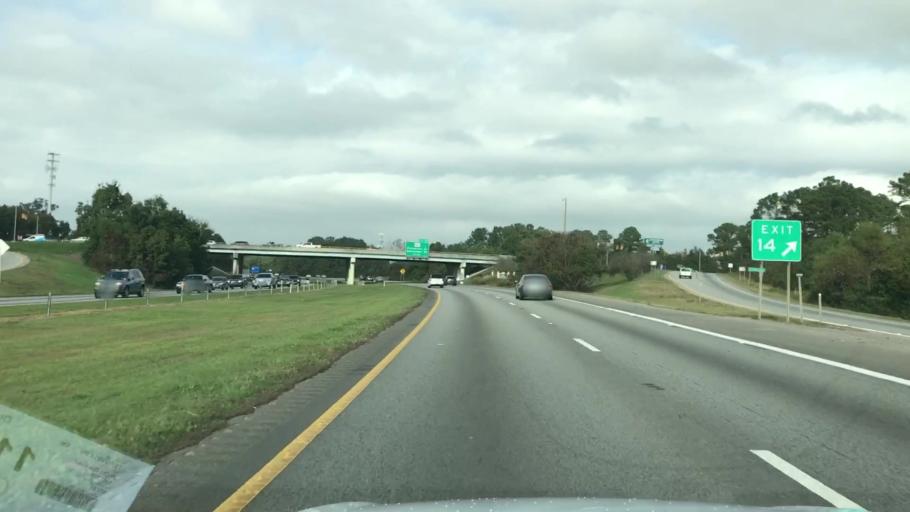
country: US
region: South Carolina
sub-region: Charleston County
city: North Charleston
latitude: 32.8404
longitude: -80.0198
